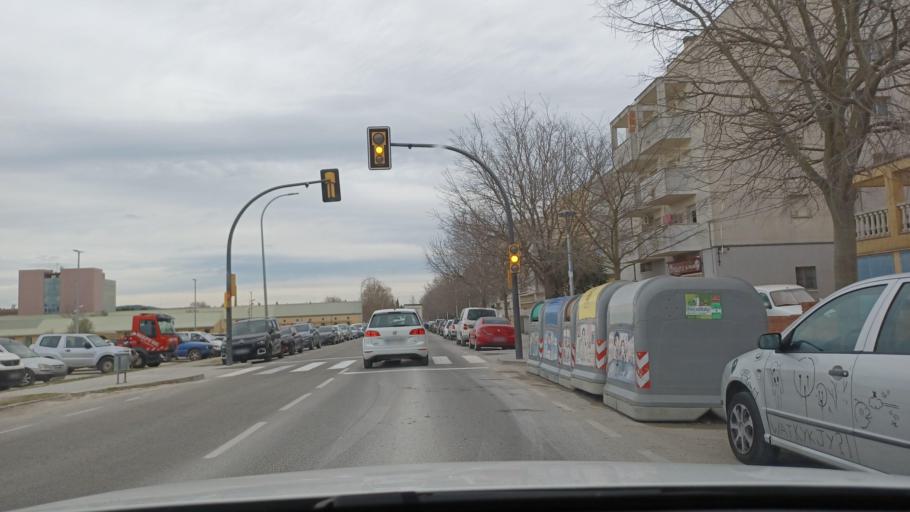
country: ES
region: Catalonia
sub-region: Provincia de Barcelona
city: Vilafranca del Penedes
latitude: 41.3569
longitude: 1.7018
